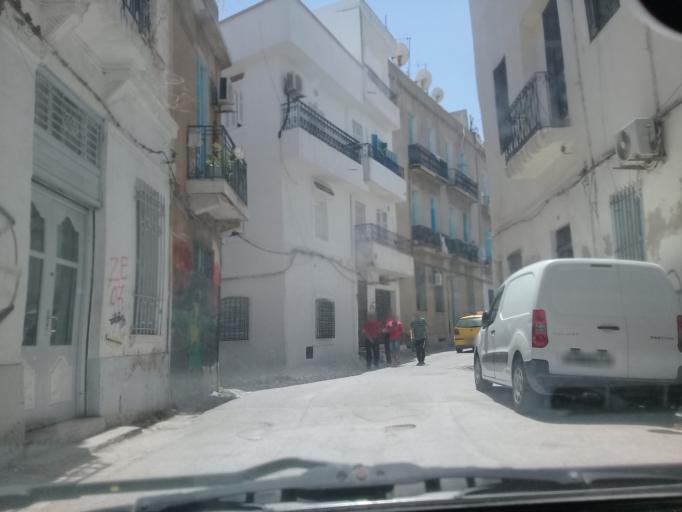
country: TN
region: Tunis
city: Tunis
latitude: 36.7917
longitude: 10.1794
